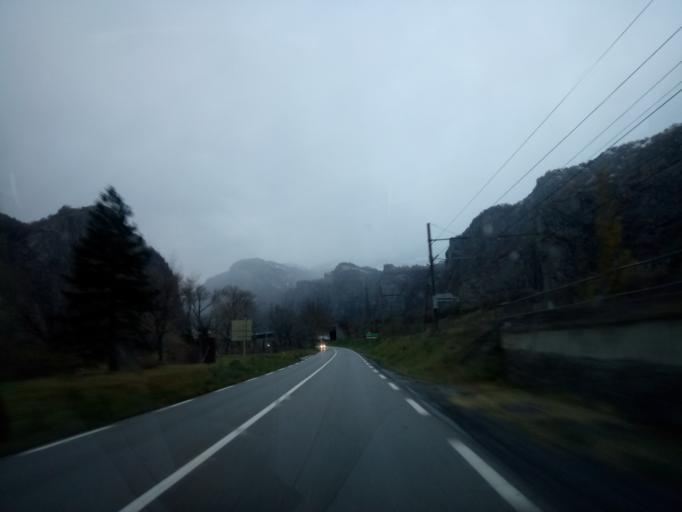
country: FR
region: Rhone-Alpes
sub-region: Departement de la Savoie
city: Saint-Jean-de-Maurienne
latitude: 45.2988
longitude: 6.3540
